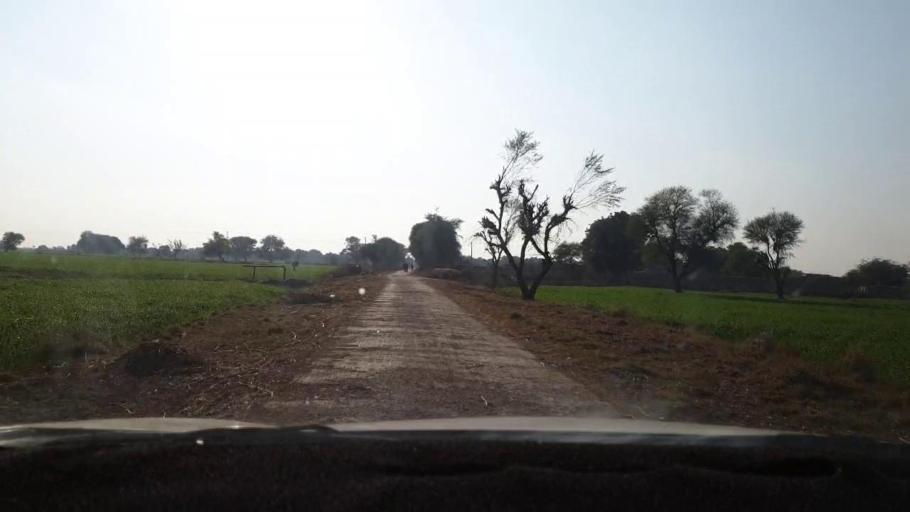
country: PK
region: Sindh
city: Berani
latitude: 25.7652
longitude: 68.7669
